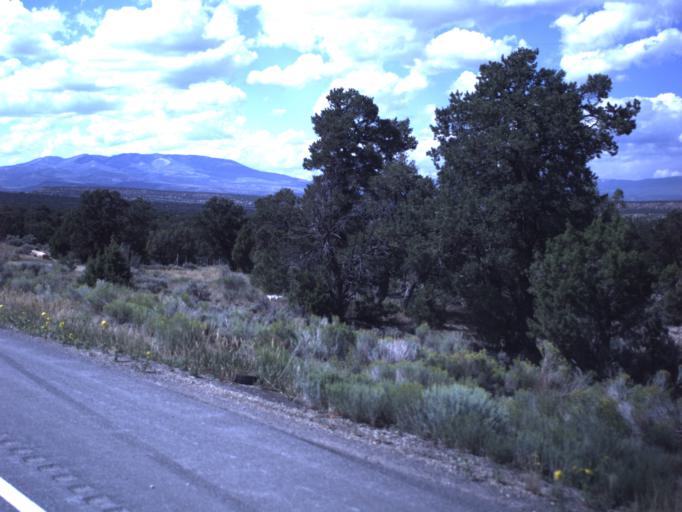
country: US
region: Utah
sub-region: Duchesne County
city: Duchesne
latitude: 40.1890
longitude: -110.6755
